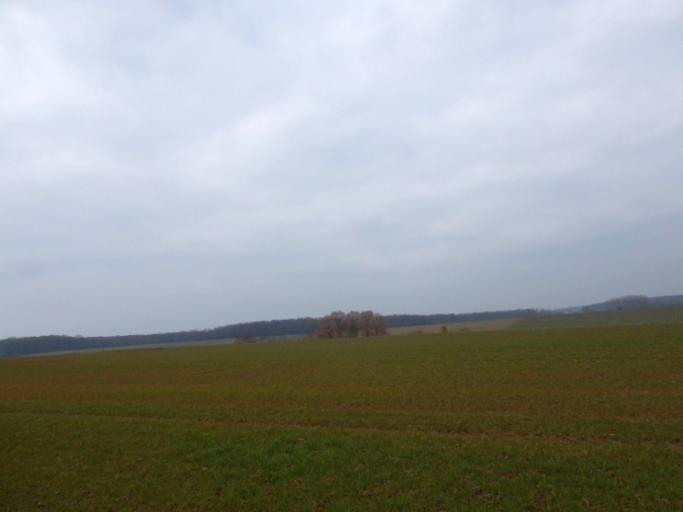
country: LU
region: Luxembourg
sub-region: Canton d'Esch-sur-Alzette
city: Mondercange
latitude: 49.5324
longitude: 5.9710
